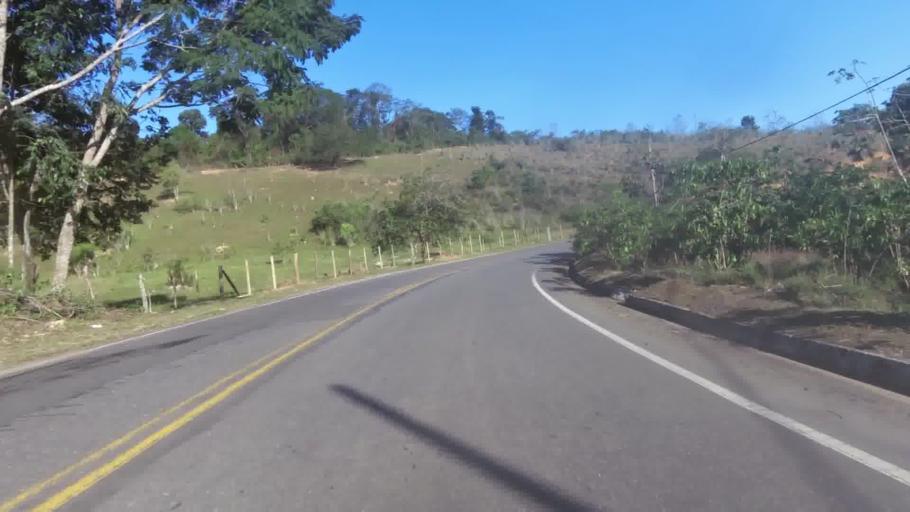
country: BR
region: Espirito Santo
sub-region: Iconha
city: Iconha
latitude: -20.7338
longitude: -40.7668
